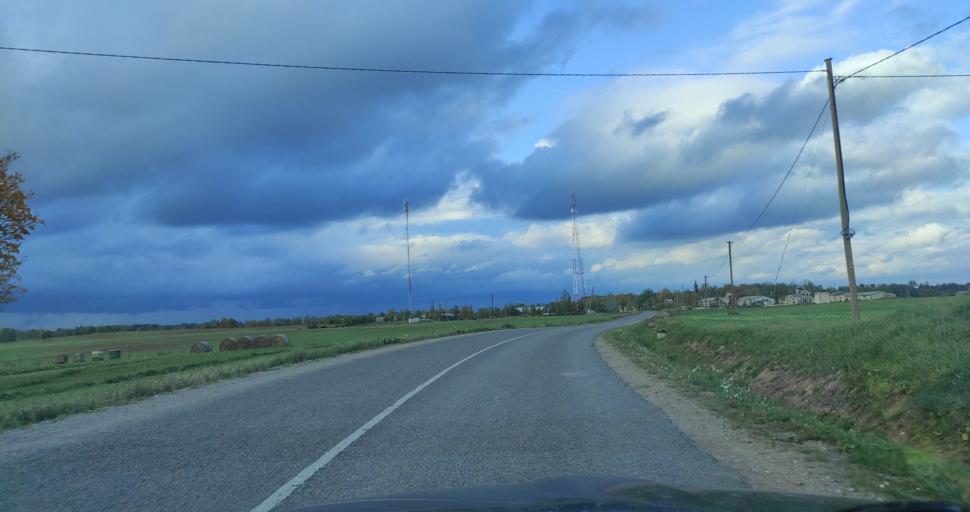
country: LV
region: Talsu Rajons
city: Sabile
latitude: 56.9412
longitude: 22.3965
